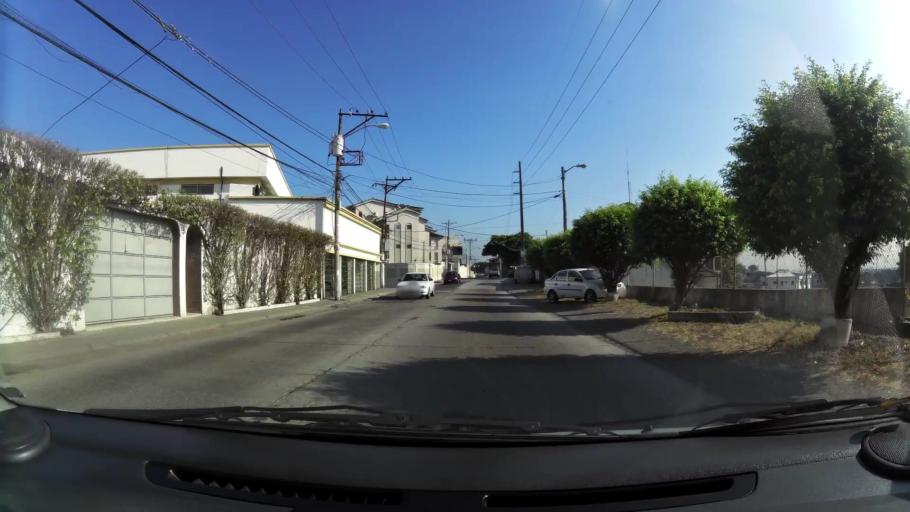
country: EC
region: Guayas
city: Guayaquil
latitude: -2.1640
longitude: -79.9073
